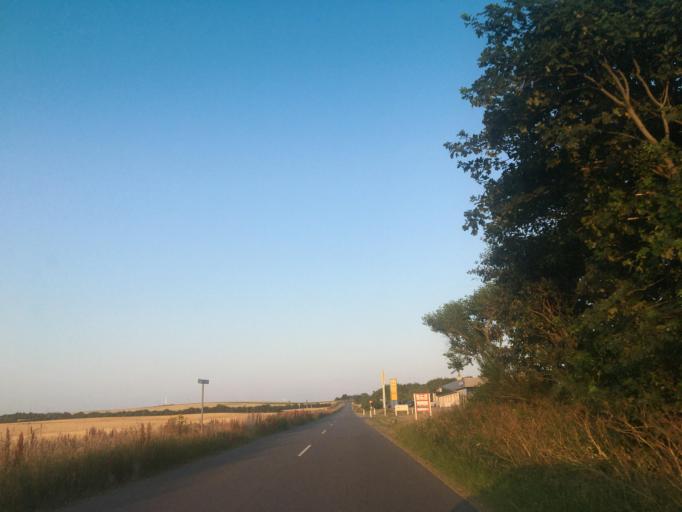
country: DK
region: North Denmark
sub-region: Thisted Kommune
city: Hurup
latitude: 56.7619
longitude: 8.3295
